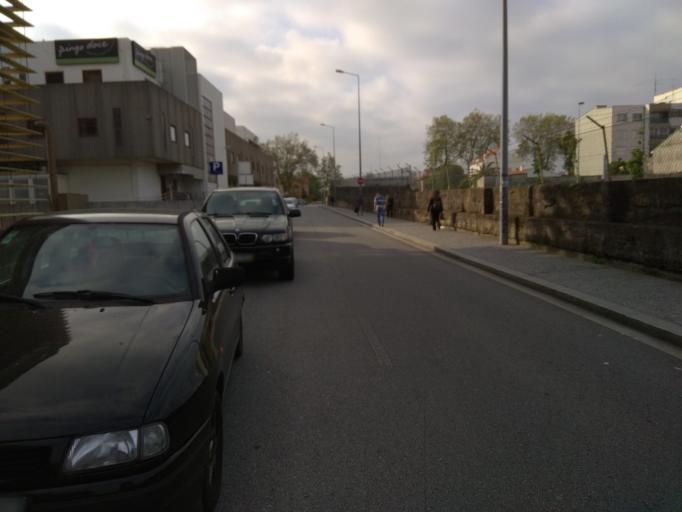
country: PT
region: Porto
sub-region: Matosinhos
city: Senhora da Hora
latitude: 41.1816
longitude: -8.6511
